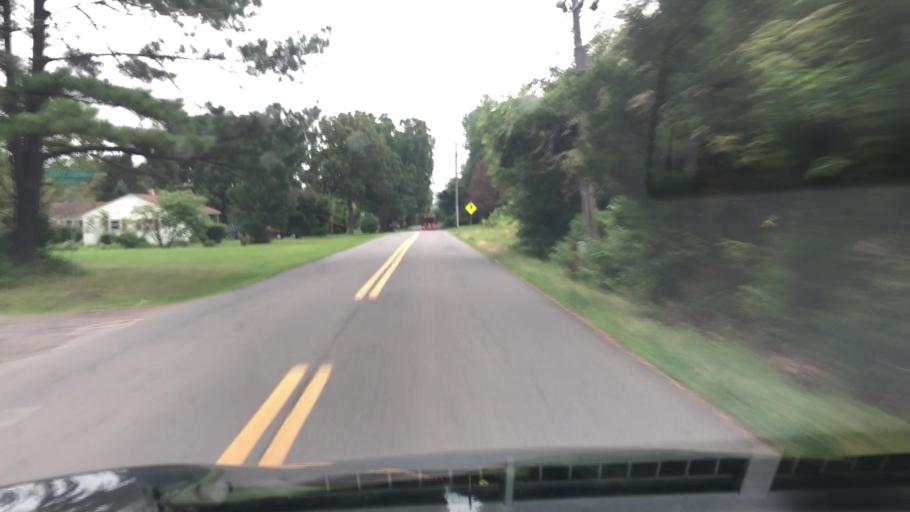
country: US
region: Virginia
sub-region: Prince William County
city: Nokesville
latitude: 38.6593
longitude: -77.6435
